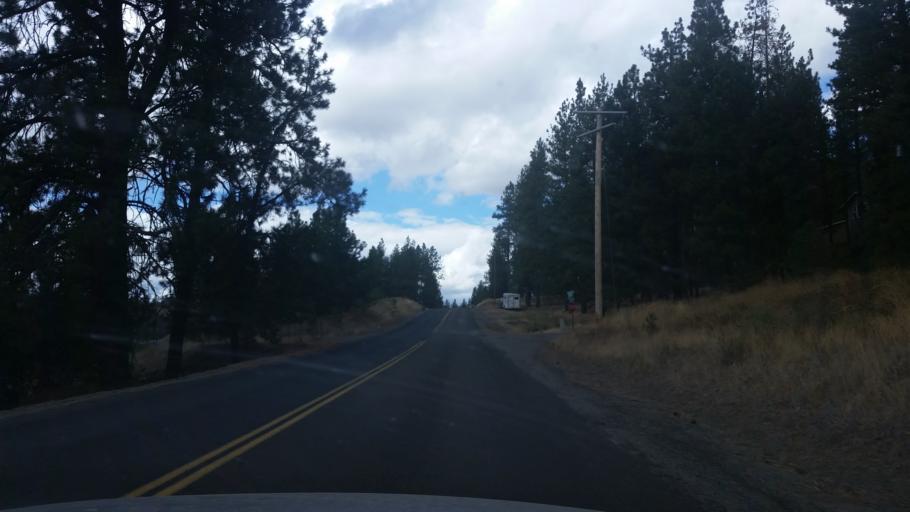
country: US
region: Washington
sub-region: Spokane County
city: Cheney
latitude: 47.5611
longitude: -117.4885
